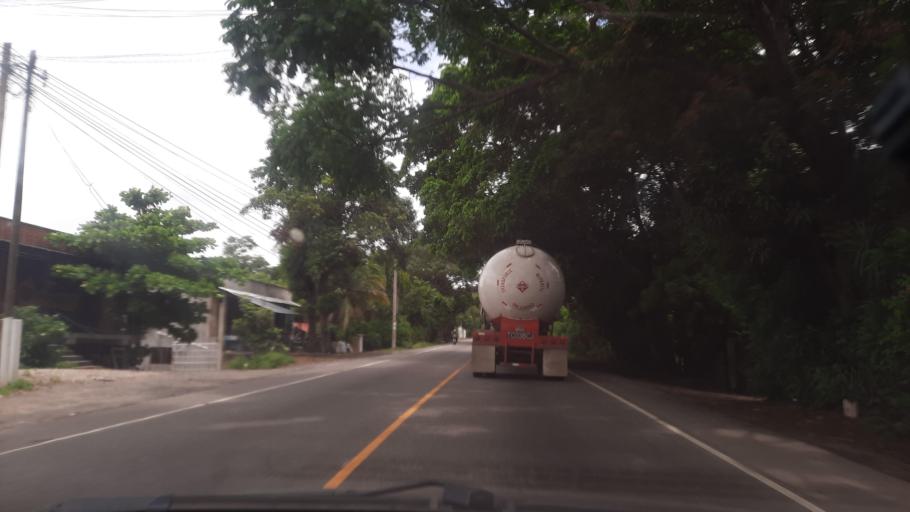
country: GT
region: Zacapa
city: Rio Hondo
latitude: 15.0699
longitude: -89.5132
